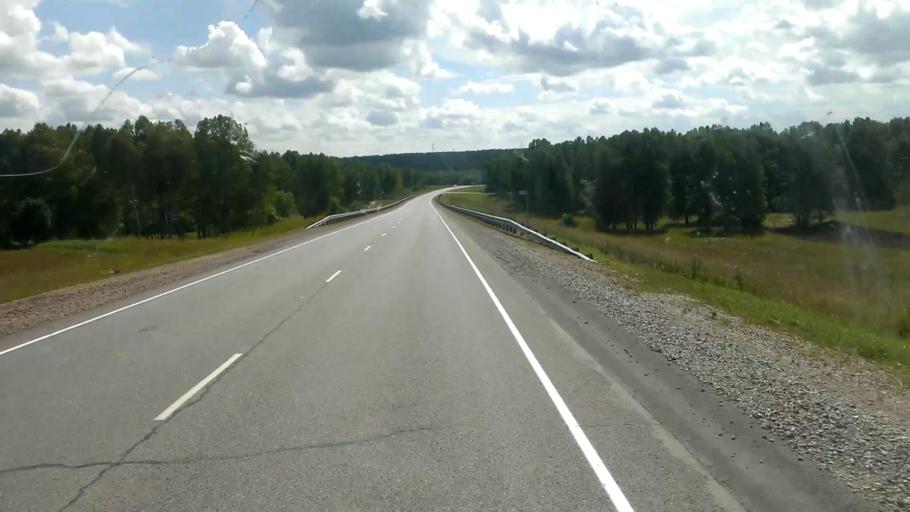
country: RU
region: Altai Krai
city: Troitskoye
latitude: 52.9423
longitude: 84.7790
